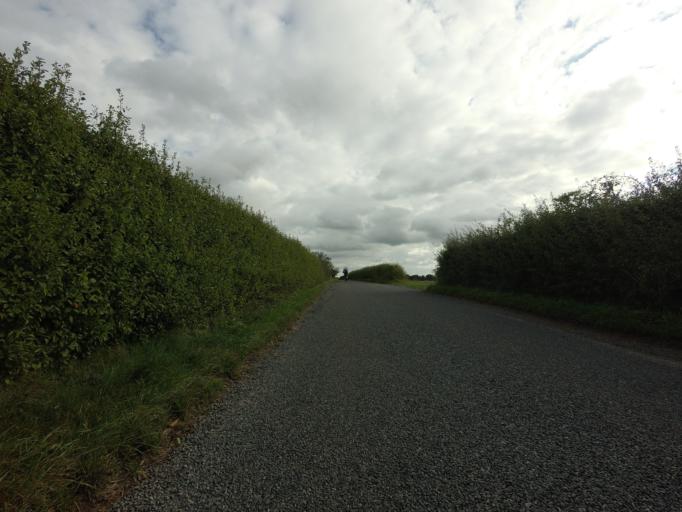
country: GB
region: England
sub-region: Norfolk
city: Dersingham
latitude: 52.8594
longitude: 0.5135
